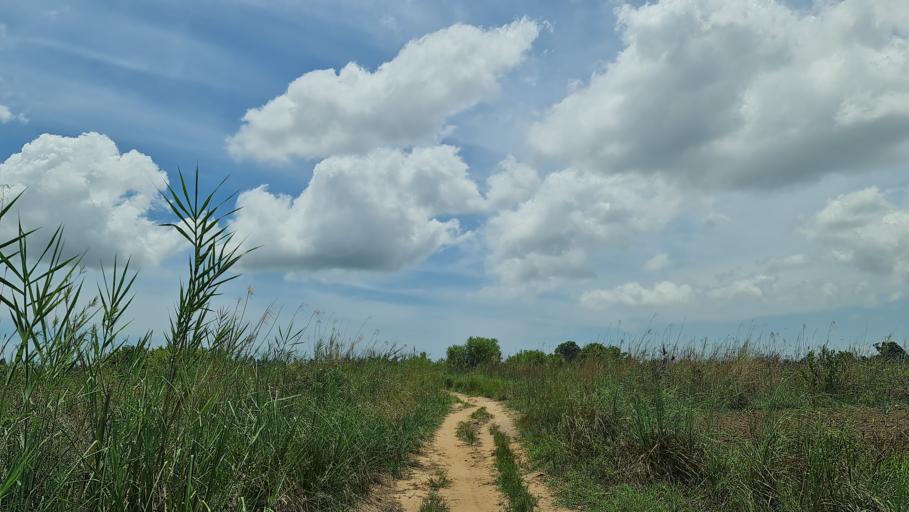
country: MZ
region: Zambezia
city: Quelimane
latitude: -17.5808
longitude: 37.3749
